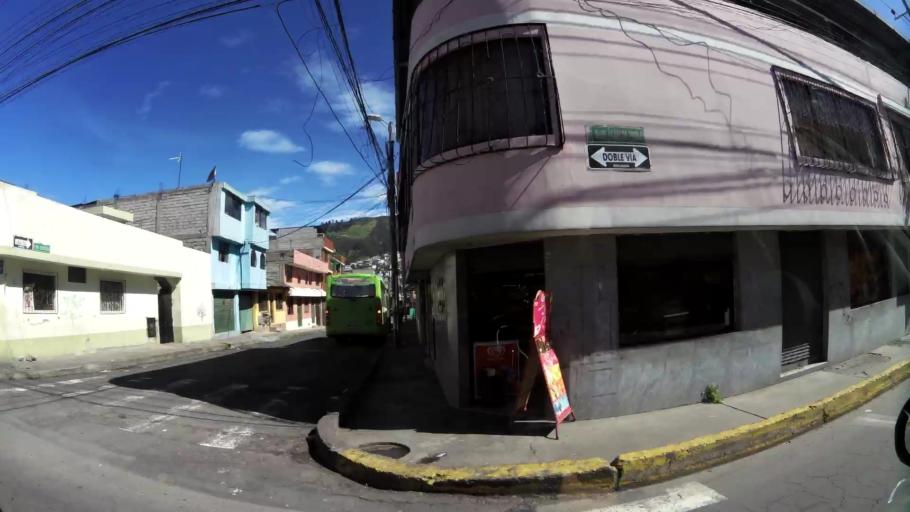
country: EC
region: Pichincha
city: Quito
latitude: -0.2795
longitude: -78.5561
